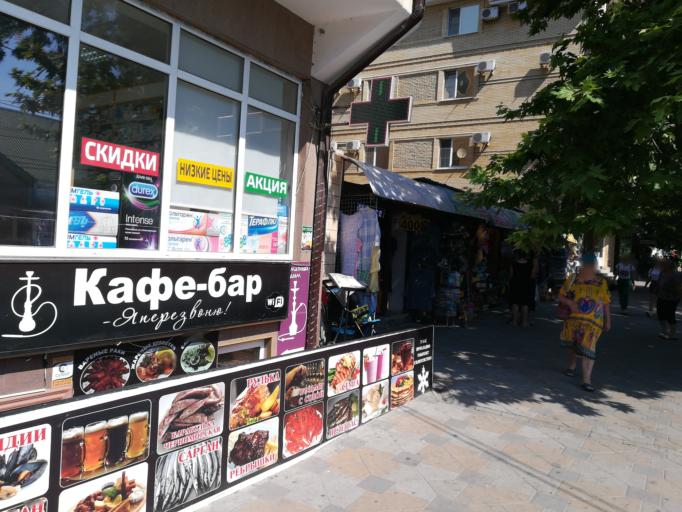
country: RU
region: Krasnodarskiy
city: Anapa
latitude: 44.8931
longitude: 37.3127
